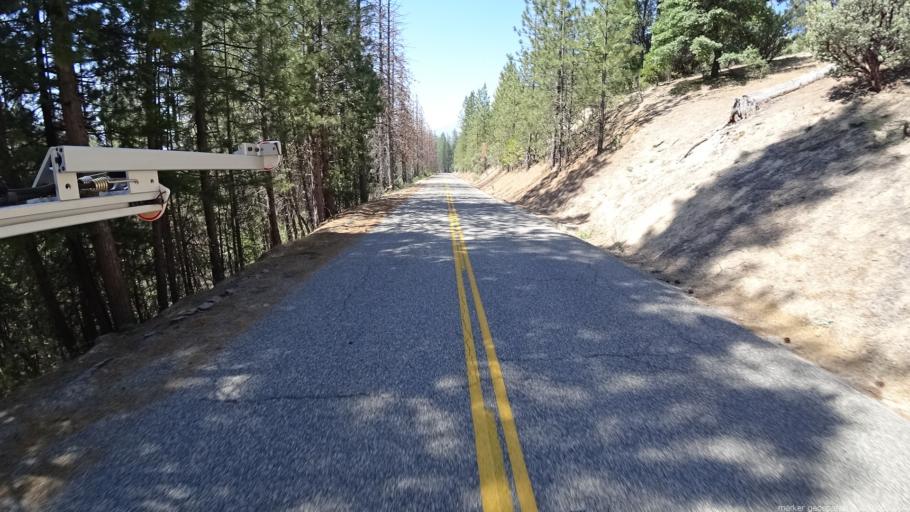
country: US
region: California
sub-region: Madera County
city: Oakhurst
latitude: 37.3994
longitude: -119.3504
